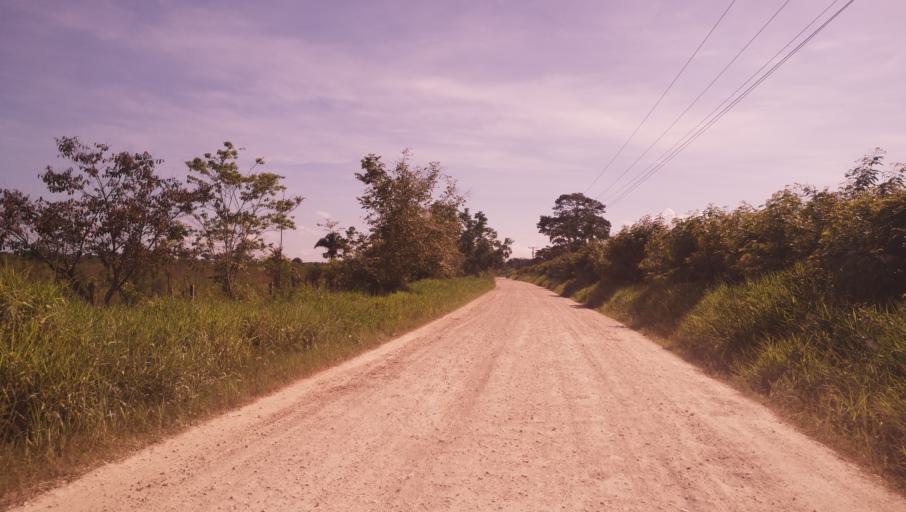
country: GT
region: Peten
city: Dolores
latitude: 16.7157
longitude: -89.3641
